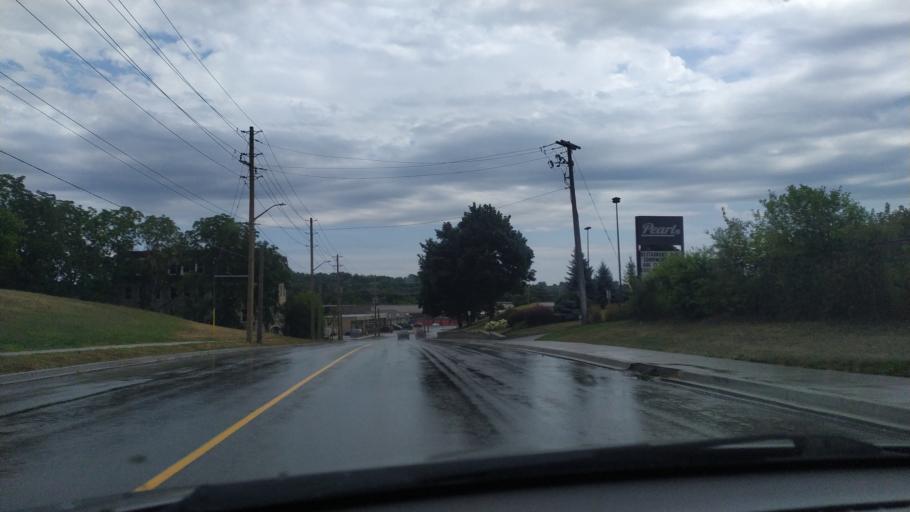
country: CA
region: Ontario
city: Waterloo
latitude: 43.4838
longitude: -80.5187
